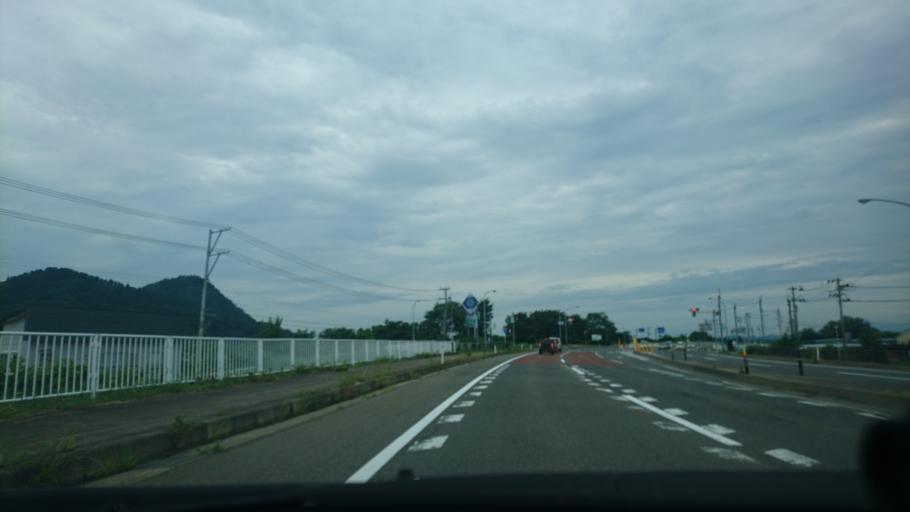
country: JP
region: Akita
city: Omagari
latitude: 39.4787
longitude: 140.4587
